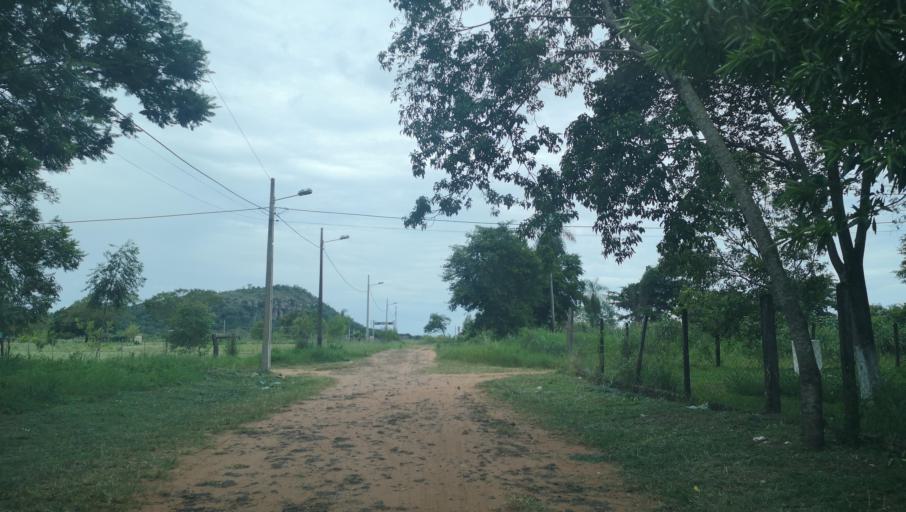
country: PY
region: San Pedro
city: Capiibary
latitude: -24.7331
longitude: -56.0177
